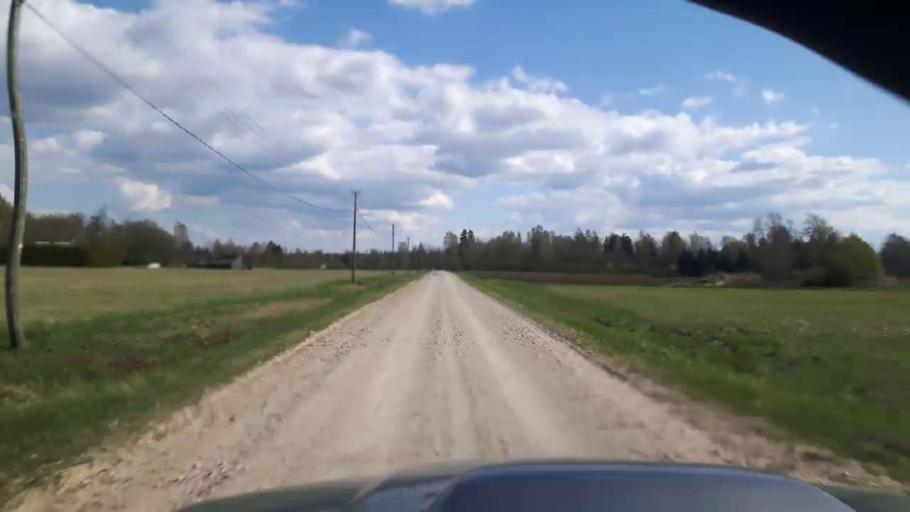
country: EE
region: Paernumaa
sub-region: Tootsi vald
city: Tootsi
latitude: 58.4626
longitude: 24.7966
